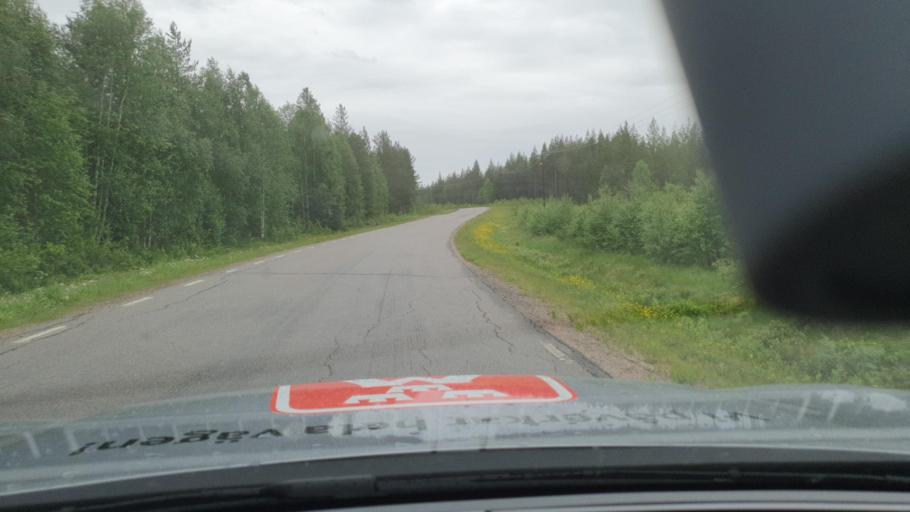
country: SE
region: Norrbotten
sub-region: Pajala Kommun
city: Pajala
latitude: 66.7692
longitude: 23.1481
